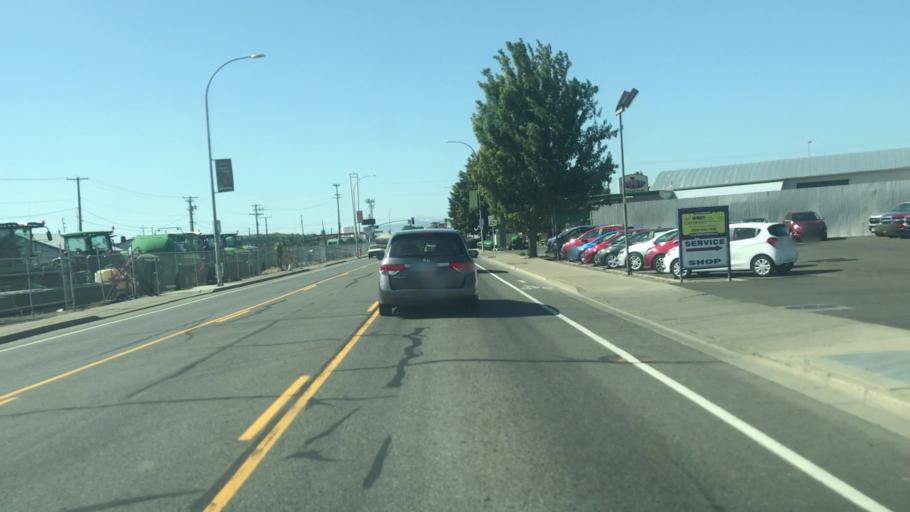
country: US
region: Washington
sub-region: Kittitas County
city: Ellensburg
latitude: 46.9826
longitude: -120.5467
